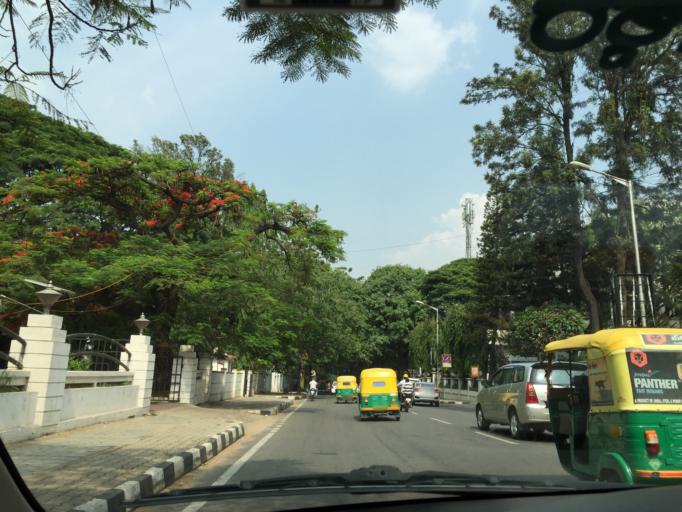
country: IN
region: Karnataka
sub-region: Bangalore Urban
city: Bangalore
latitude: 12.9840
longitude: 77.5933
